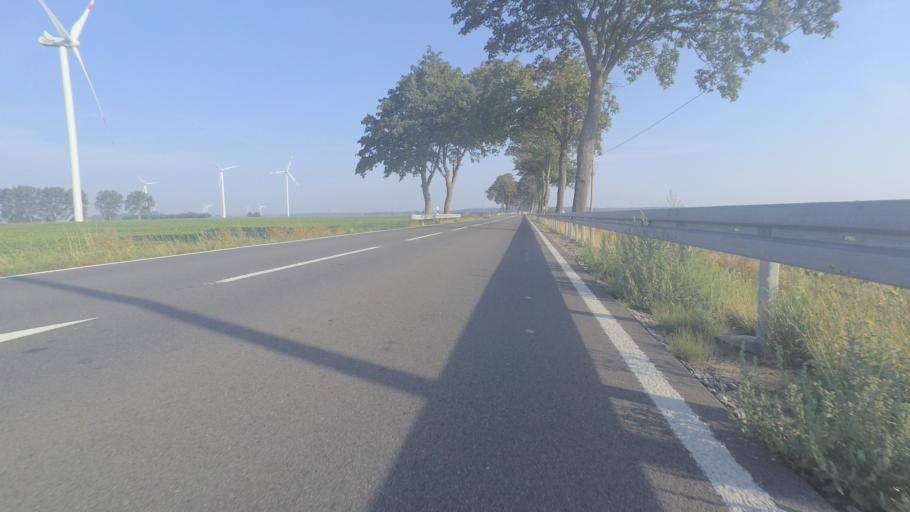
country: DE
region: Mecklenburg-Vorpommern
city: Gormin
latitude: 54.0079
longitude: 13.1425
